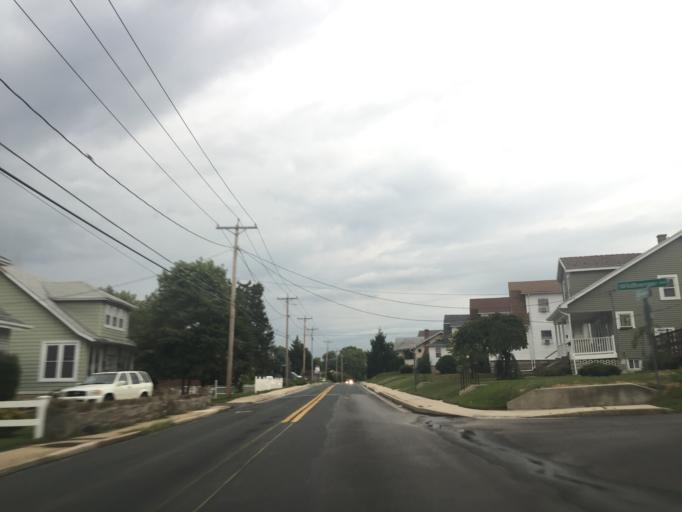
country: US
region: Maryland
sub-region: Baltimore County
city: Parkville
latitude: 39.3768
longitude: -76.5461
